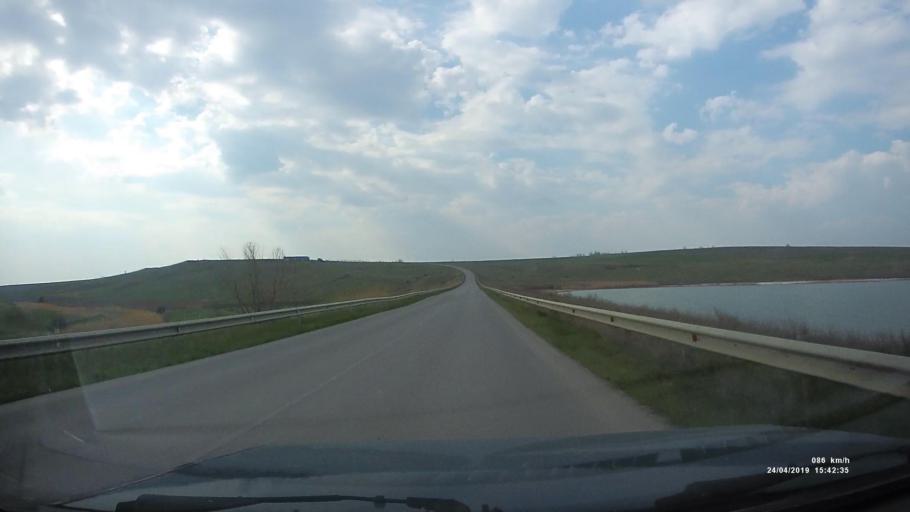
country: RU
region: Kalmykiya
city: Yashalta
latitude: 46.5773
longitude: 42.7859
